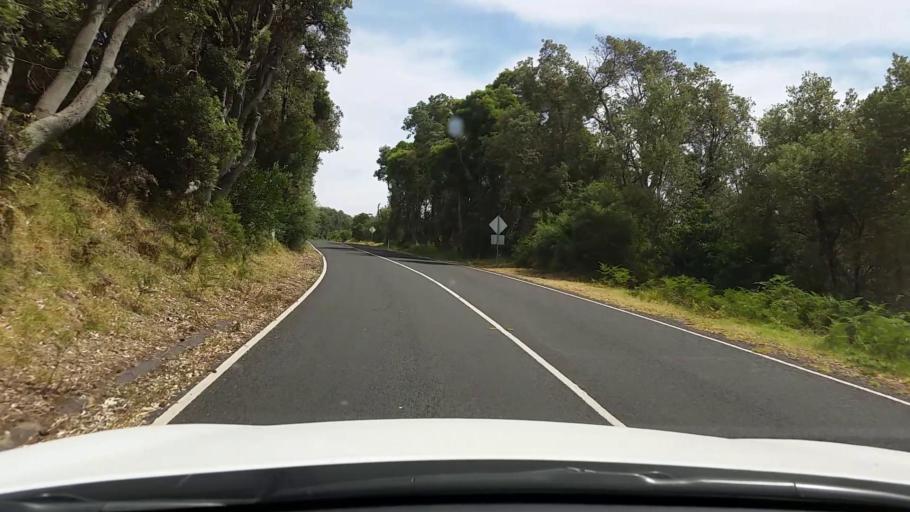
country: AU
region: Victoria
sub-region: Mornington Peninsula
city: Rosebud
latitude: -38.4766
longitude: 144.9317
